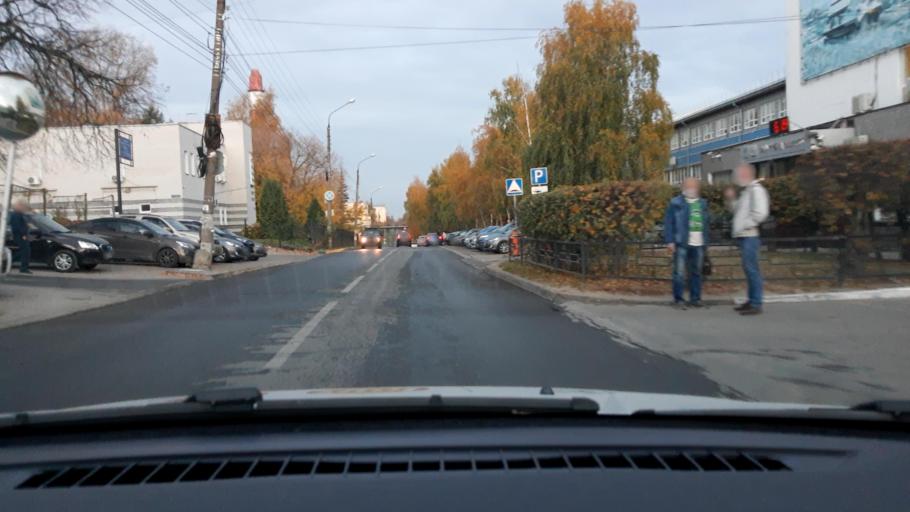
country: RU
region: Nizjnij Novgorod
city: Nizhniy Novgorod
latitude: 56.2501
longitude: 43.9778
